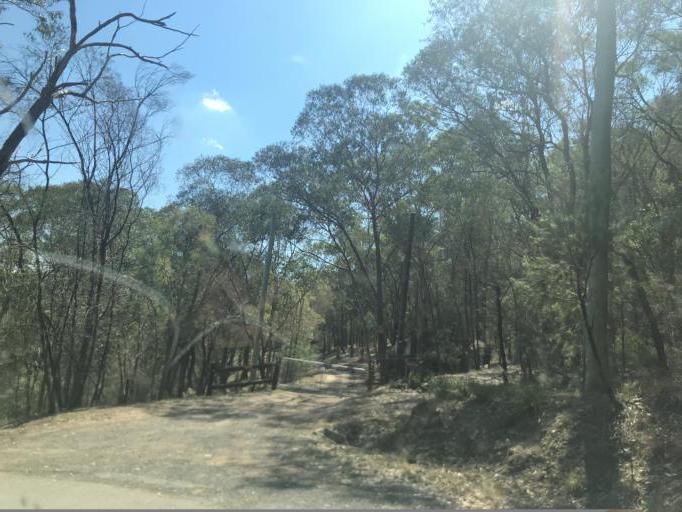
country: AU
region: New South Wales
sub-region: Hawkesbury
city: Pitt Town
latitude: -33.4141
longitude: 150.9199
